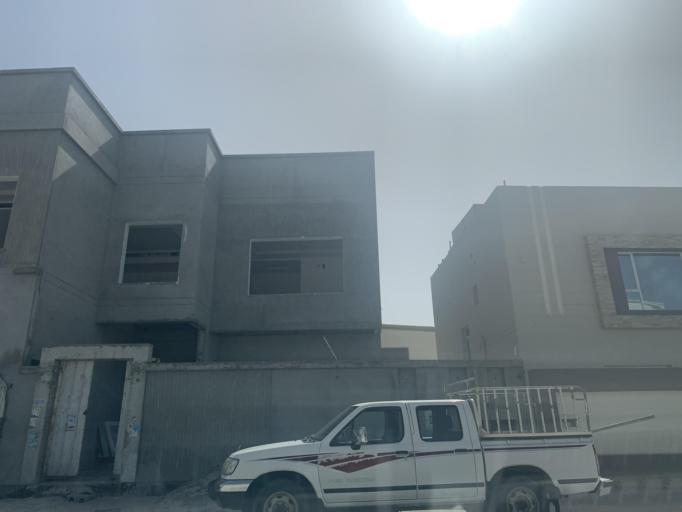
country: BH
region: Northern
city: Sitrah
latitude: 26.1681
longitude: 50.6191
